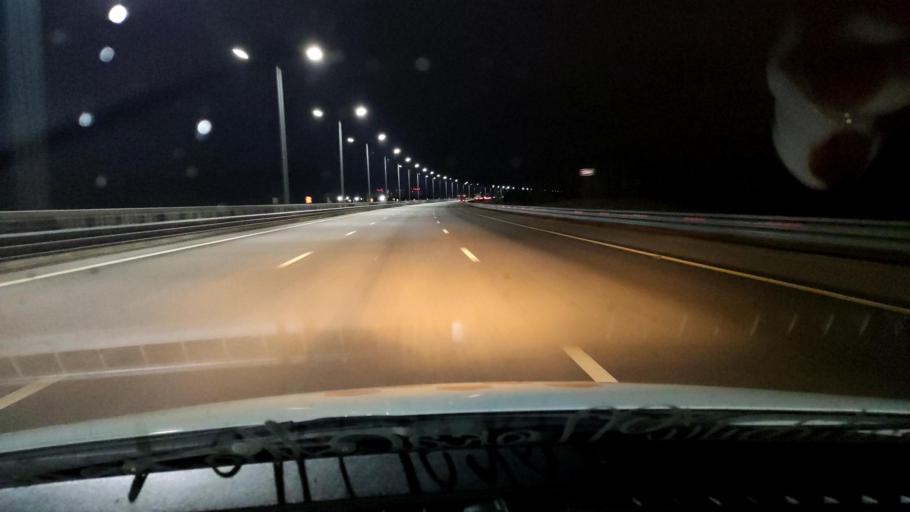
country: RU
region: Voronezj
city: Somovo
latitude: 51.7636
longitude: 39.3061
